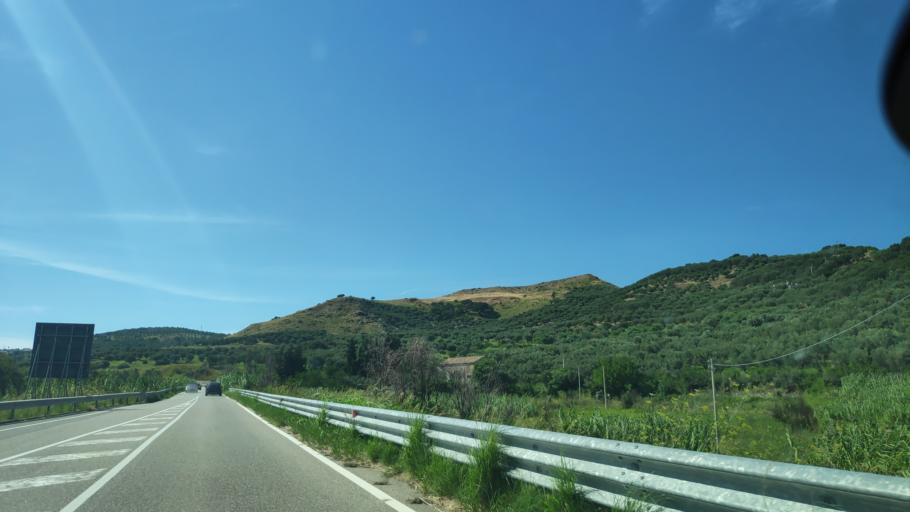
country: IT
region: Calabria
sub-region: Provincia di Catanzaro
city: Staletti
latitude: 38.7833
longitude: 16.5492
